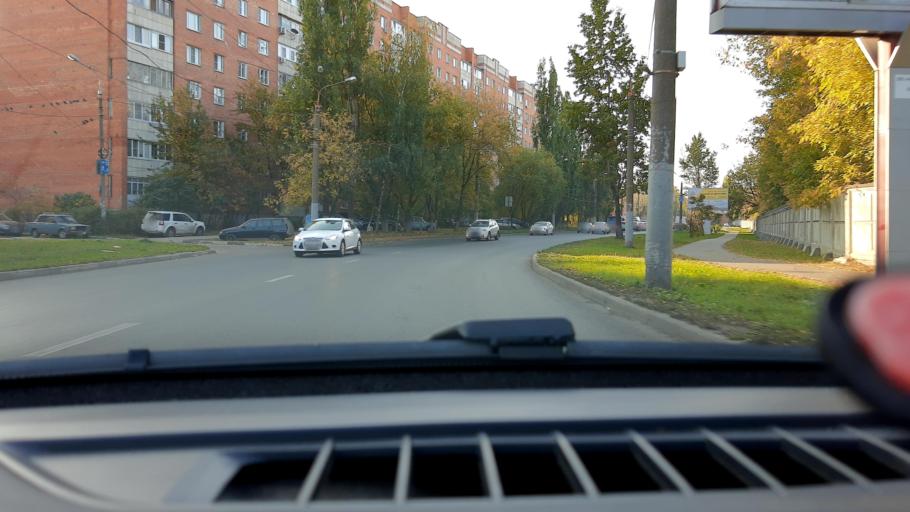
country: RU
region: Nizjnij Novgorod
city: Nizhniy Novgorod
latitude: 56.3283
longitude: 43.8678
